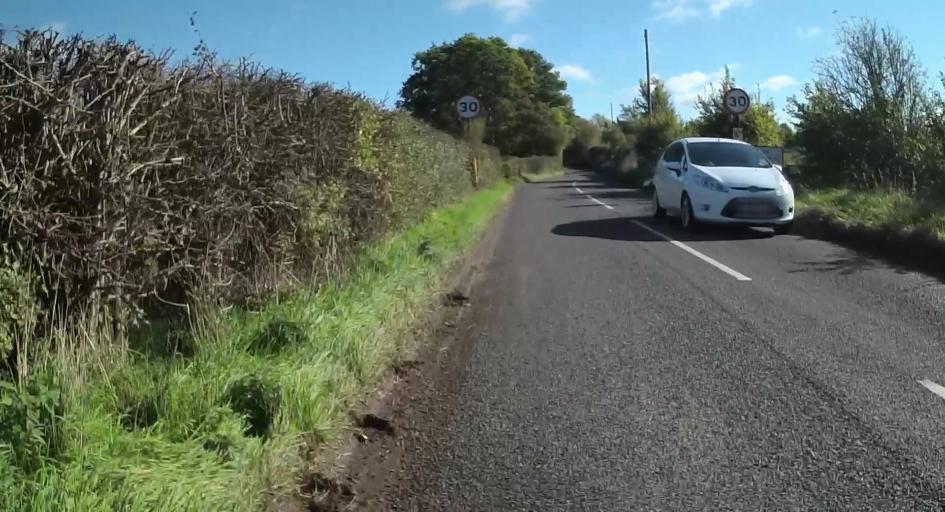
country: GB
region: England
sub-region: Hampshire
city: Old Basing
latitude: 51.2637
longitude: -1.0037
